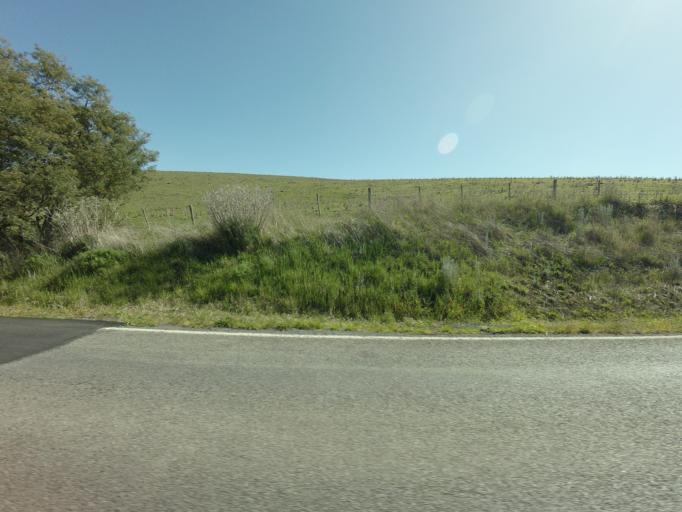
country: AU
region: Tasmania
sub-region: Derwent Valley
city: New Norfolk
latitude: -42.6376
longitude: 146.9175
